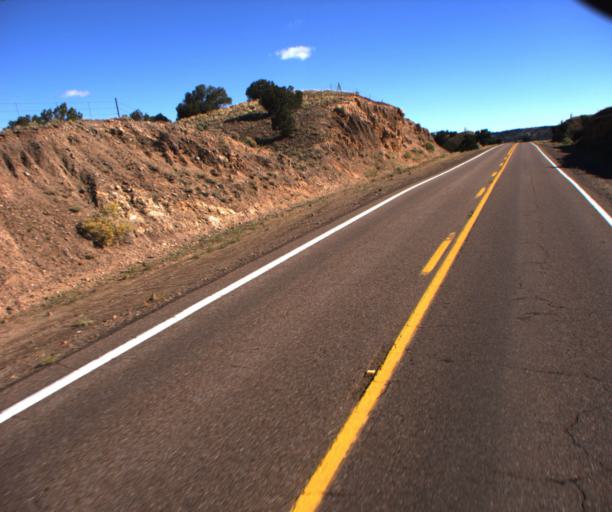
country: US
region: Arizona
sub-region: Apache County
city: Saint Johns
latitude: 34.4835
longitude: -109.5877
